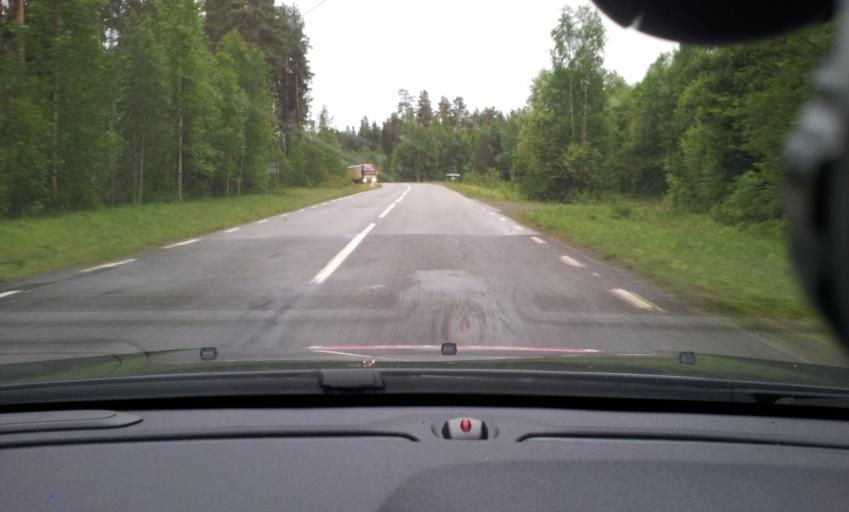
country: SE
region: Jaemtland
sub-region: Stroemsunds Kommun
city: Stroemsund
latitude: 63.3903
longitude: 15.6745
